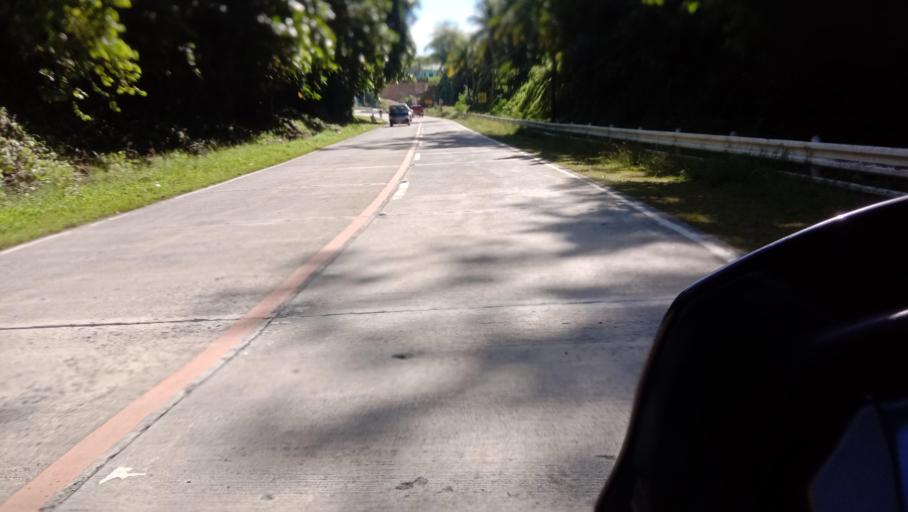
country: PH
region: Caraga
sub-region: Province of Surigao del Sur
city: Barobo
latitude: 8.5403
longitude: 126.1100
